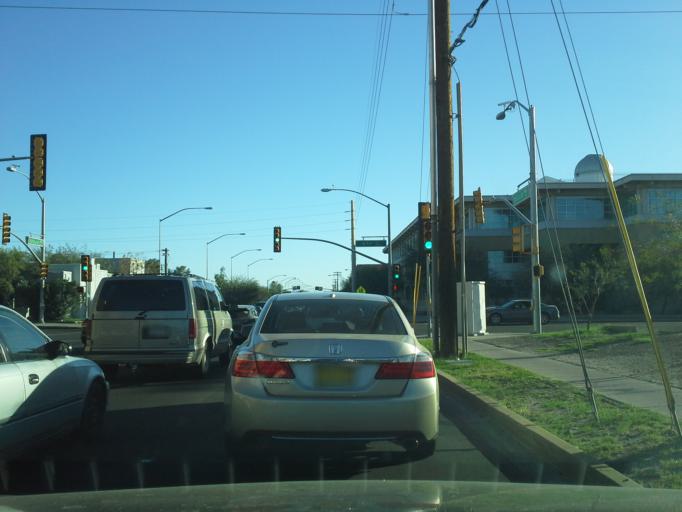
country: US
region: Arizona
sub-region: Pima County
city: South Tucson
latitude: 32.2281
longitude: -110.9596
